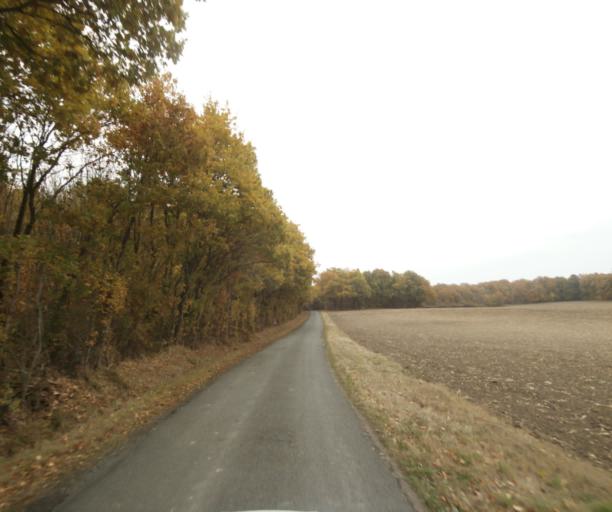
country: FR
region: Poitou-Charentes
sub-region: Departement de la Charente-Maritime
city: Chermignac
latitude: 45.7109
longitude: -0.6736
